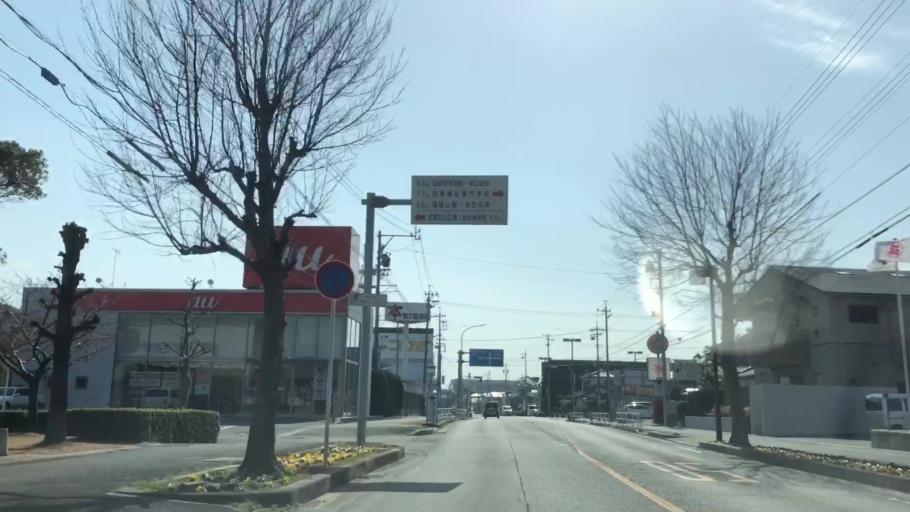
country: JP
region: Aichi
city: Tahara
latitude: 34.6752
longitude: 137.2717
